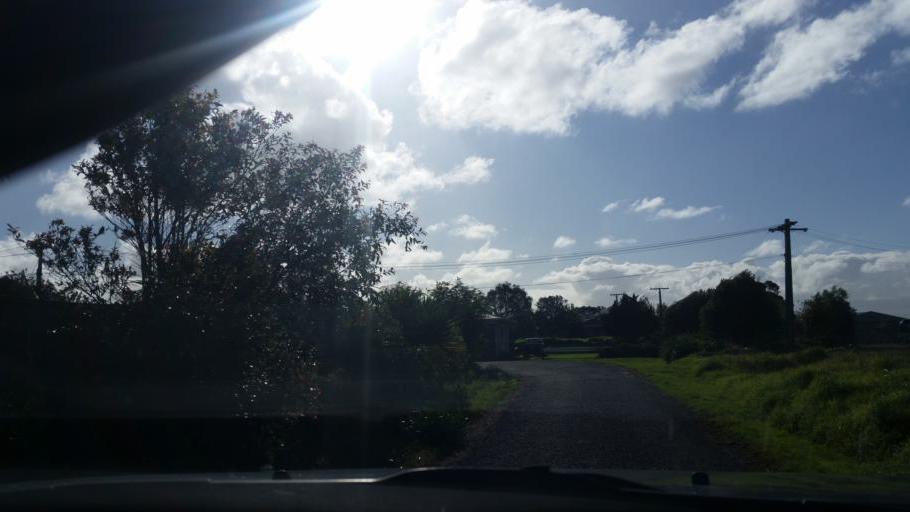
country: NZ
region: Northland
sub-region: Kaipara District
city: Dargaville
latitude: -36.0302
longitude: 173.9261
